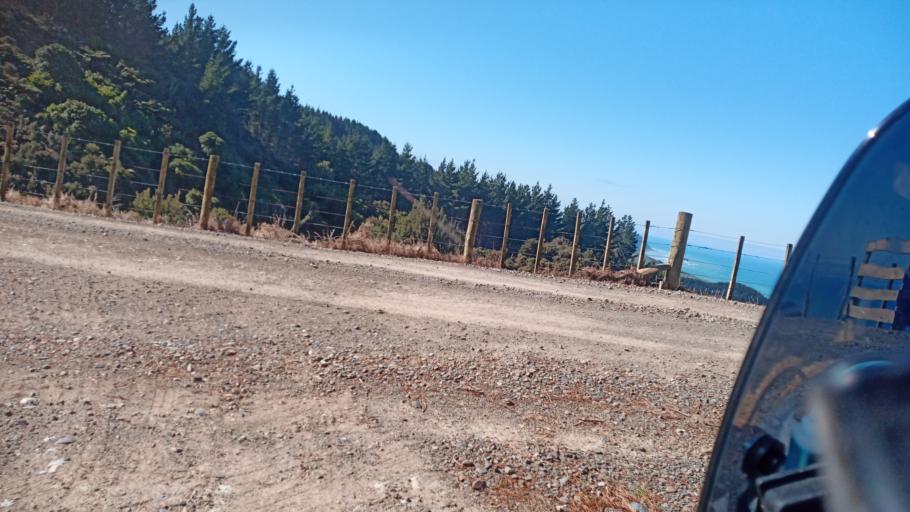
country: NZ
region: Gisborne
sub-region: Gisborne District
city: Gisborne
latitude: -39.1749
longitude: 177.9049
